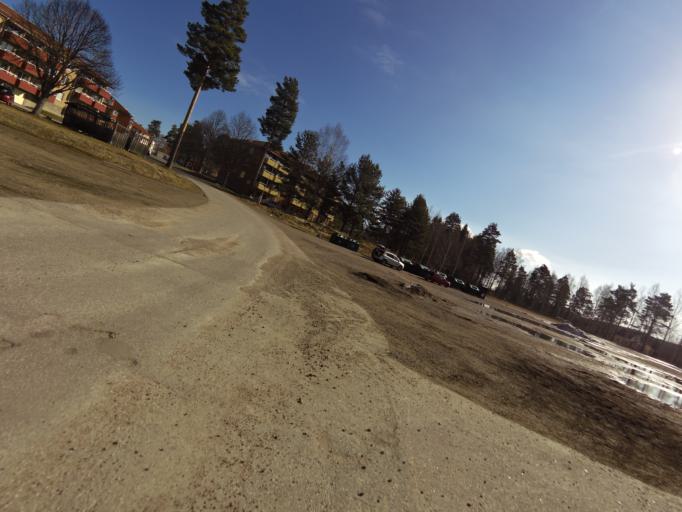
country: SE
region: Gaevleborg
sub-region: Hofors Kommun
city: Hofors
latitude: 60.5427
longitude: 16.2713
